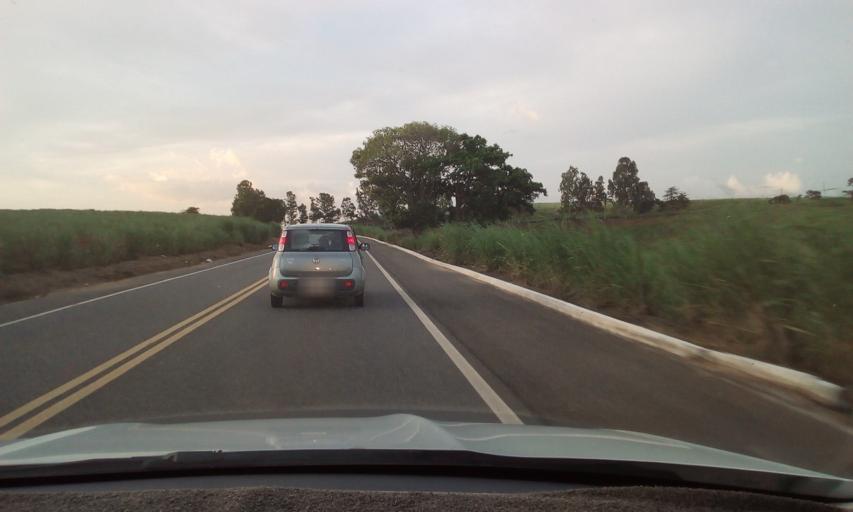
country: BR
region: Pernambuco
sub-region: Vicencia
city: Vicencia
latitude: -7.6030
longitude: -35.2409
